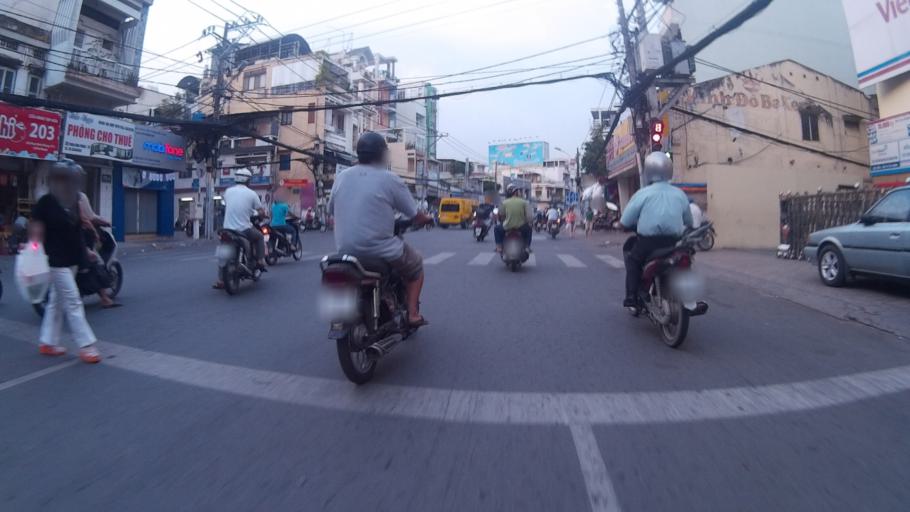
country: VN
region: Ho Chi Minh City
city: Quan Phu Nhuan
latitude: 10.7957
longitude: 106.6822
